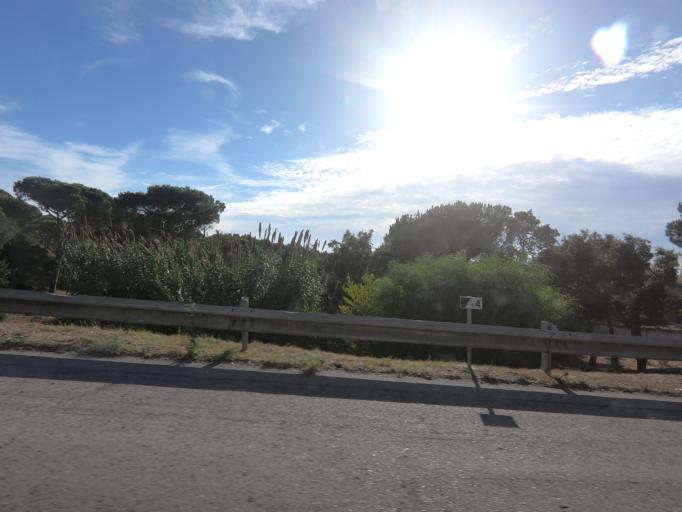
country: PT
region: Setubal
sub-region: Barreiro
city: Santo Antonio da Charneca
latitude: 38.6293
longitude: -9.0393
